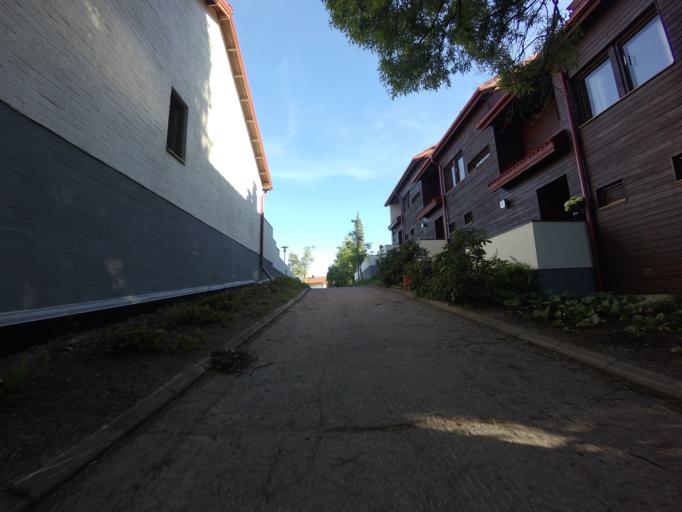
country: FI
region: Uusimaa
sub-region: Helsinki
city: Koukkuniemi
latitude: 60.1711
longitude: 24.7421
